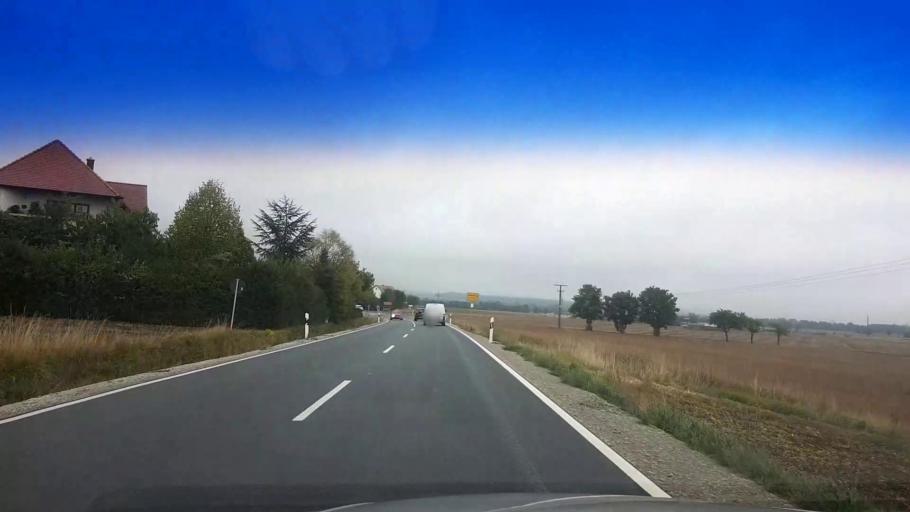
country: DE
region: Bavaria
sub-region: Upper Franconia
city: Buttenheim
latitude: 49.7880
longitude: 11.0415
